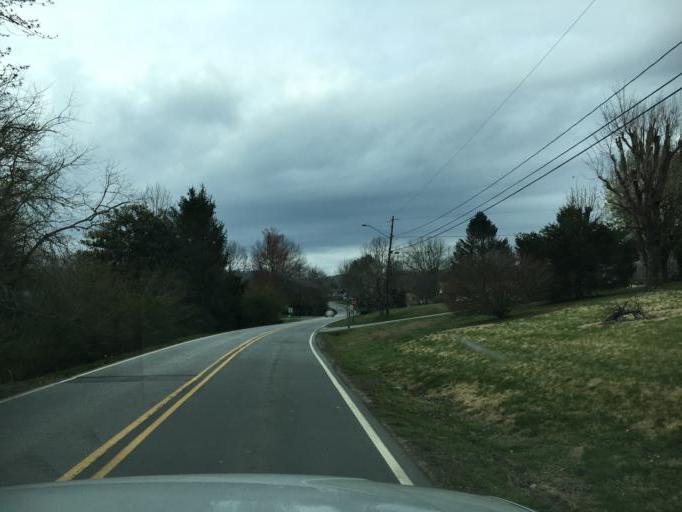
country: US
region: North Carolina
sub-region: Transylvania County
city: Brevard
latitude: 35.2384
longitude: -82.7194
